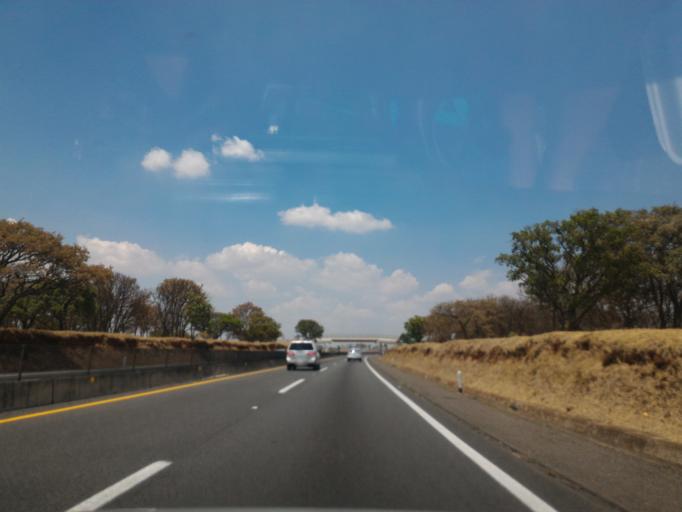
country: MX
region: Jalisco
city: Tepatitlan de Morelos
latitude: 20.8660
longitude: -102.7578
